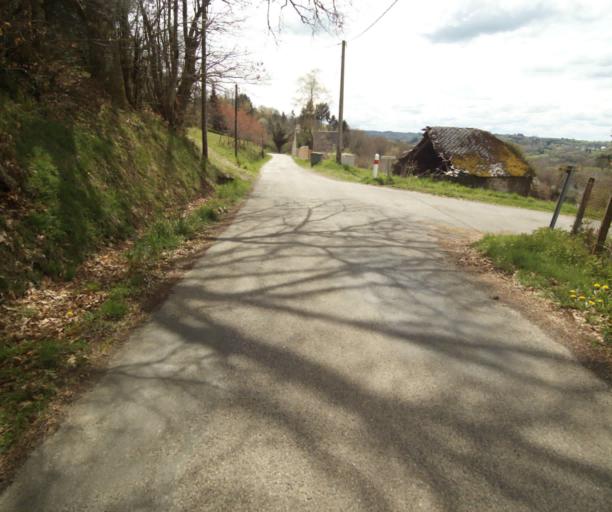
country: FR
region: Limousin
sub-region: Departement de la Correze
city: Laguenne
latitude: 45.2404
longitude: 1.8629
